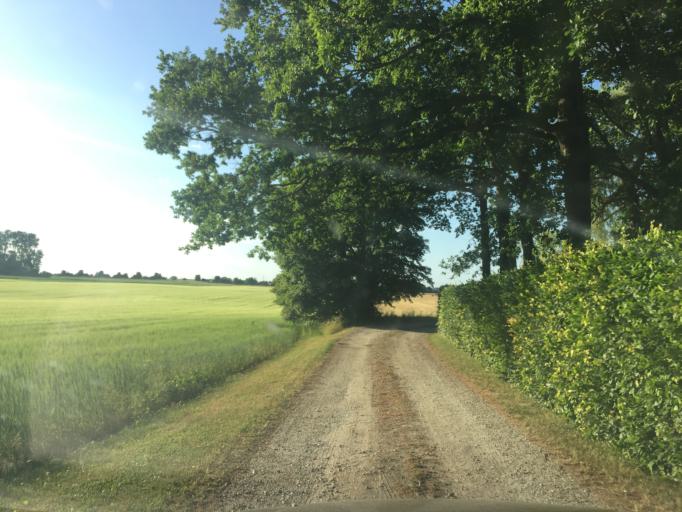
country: DK
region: Capital Region
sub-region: Hoje-Taastrup Kommune
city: Taastrup
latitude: 55.6794
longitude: 12.2797
